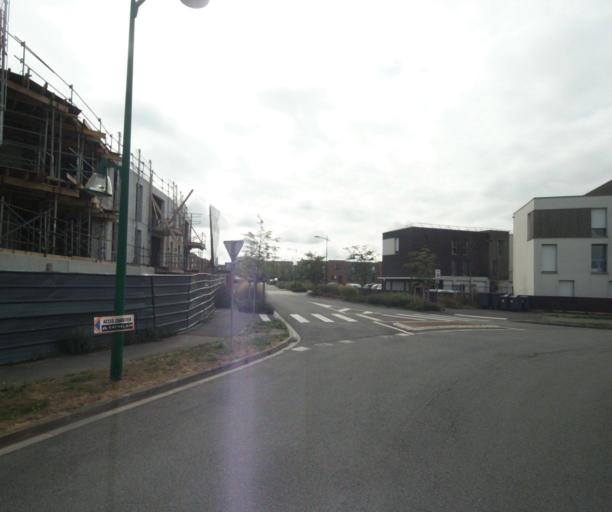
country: FR
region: Nord-Pas-de-Calais
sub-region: Departement du Nord
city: Ronchin
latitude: 50.5855
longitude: 3.0983
